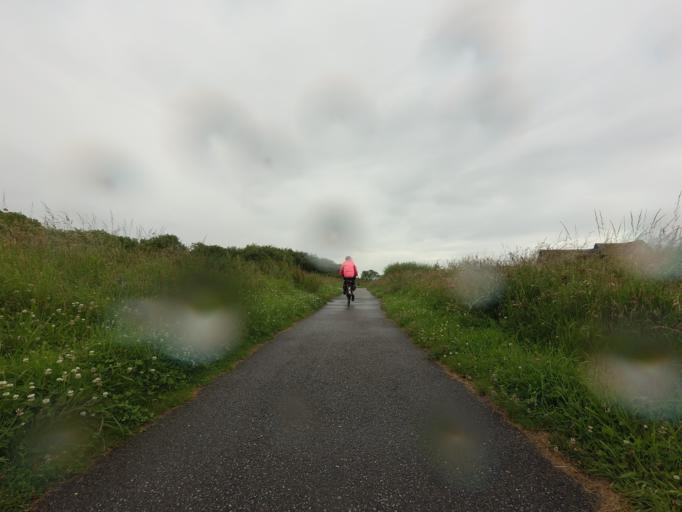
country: GB
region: Scotland
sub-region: Moray
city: Buckie
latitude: 57.6846
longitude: -2.9338
